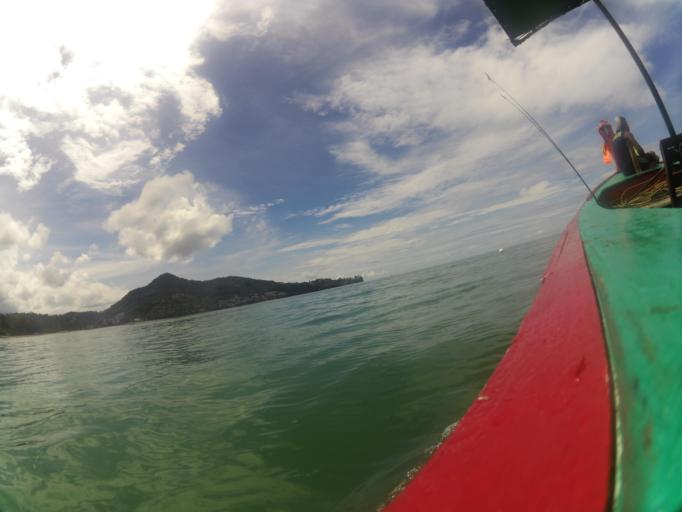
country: TH
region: Phuket
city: Patong
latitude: 7.9619
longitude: 98.2823
